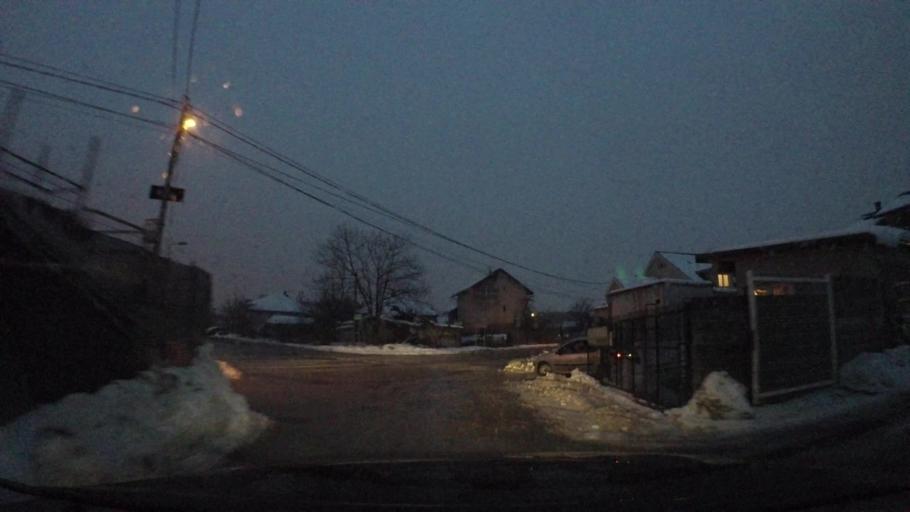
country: BA
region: Federation of Bosnia and Herzegovina
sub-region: Kanton Sarajevo
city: Sarajevo
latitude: 43.8452
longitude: 18.3207
